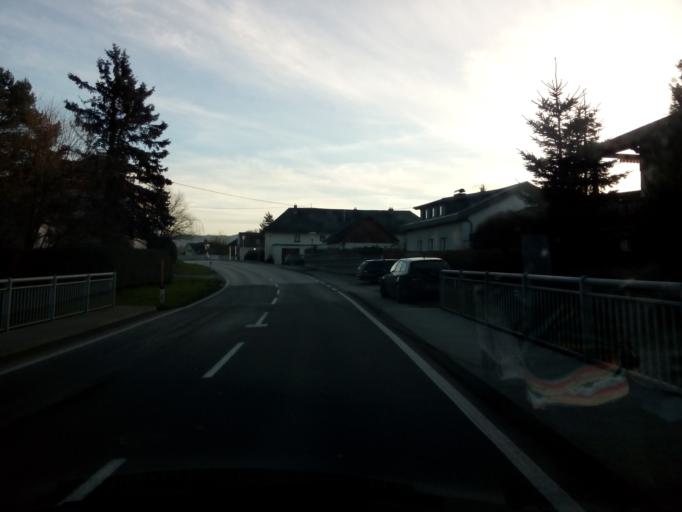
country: AT
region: Upper Austria
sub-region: Politischer Bezirk Kirchdorf an der Krems
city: Kremsmunster
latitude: 47.9869
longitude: 14.1240
